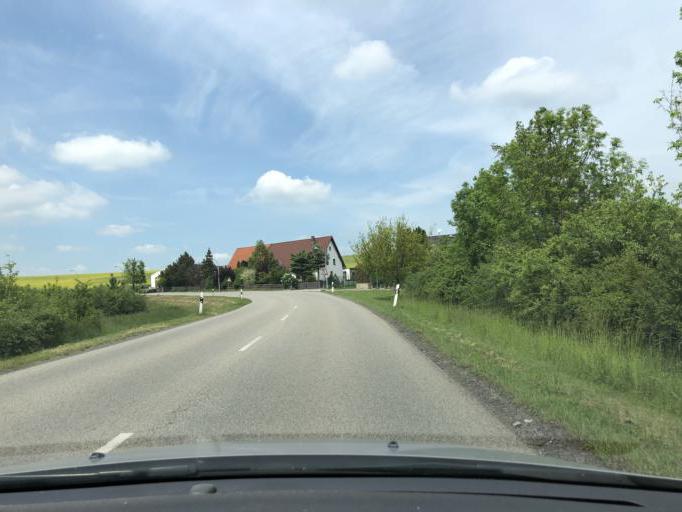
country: DE
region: Thuringia
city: Saara
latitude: 50.9533
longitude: 12.4266
